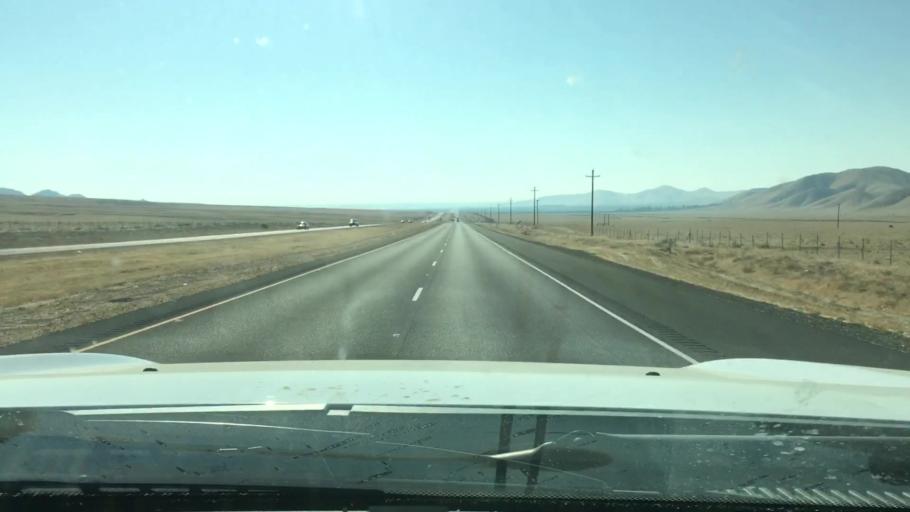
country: US
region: California
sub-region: San Luis Obispo County
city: Shandon
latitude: 35.7066
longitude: -120.1568
